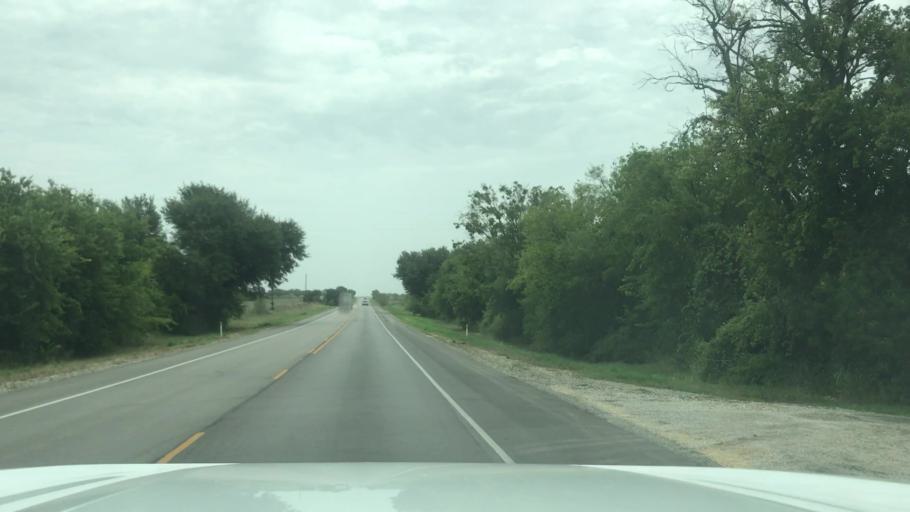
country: US
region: Texas
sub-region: Erath County
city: Dublin
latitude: 32.0842
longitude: -98.2512
